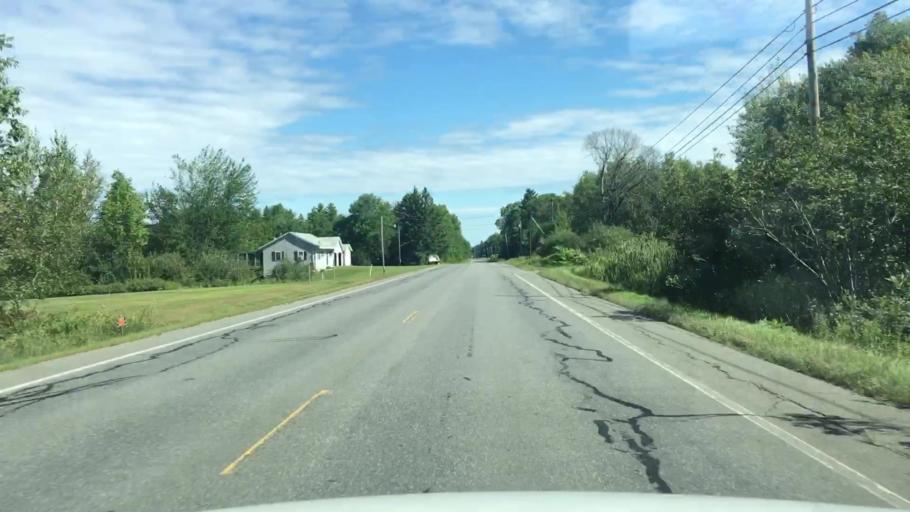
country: US
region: Maine
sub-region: Penobscot County
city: Dexter
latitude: 45.0617
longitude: -69.2485
